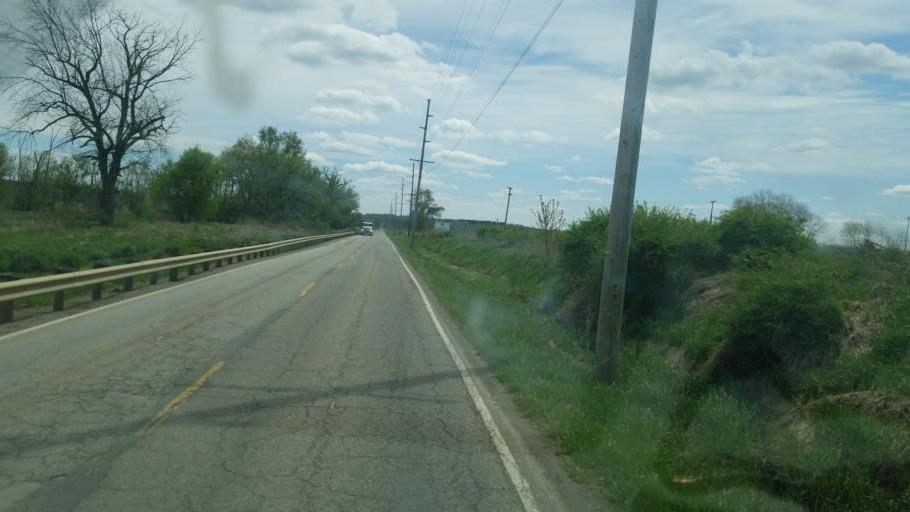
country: US
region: Ohio
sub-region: Wayne County
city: Wooster
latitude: 40.7567
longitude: -81.9443
